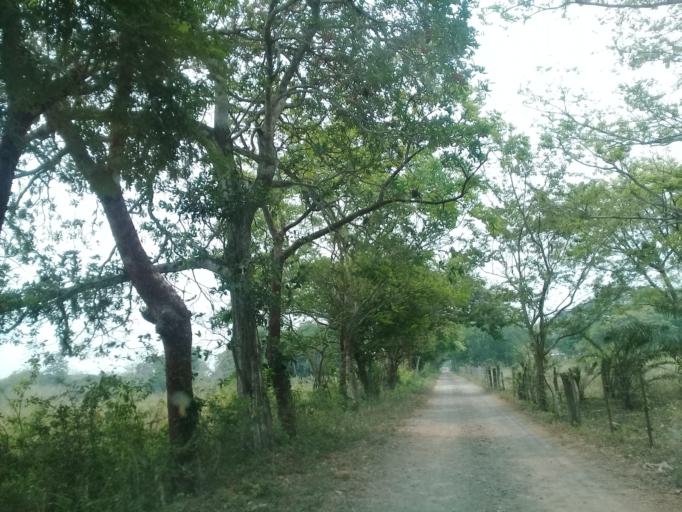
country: MX
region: Veracruz
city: Jamapa
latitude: 18.9555
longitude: -96.1989
